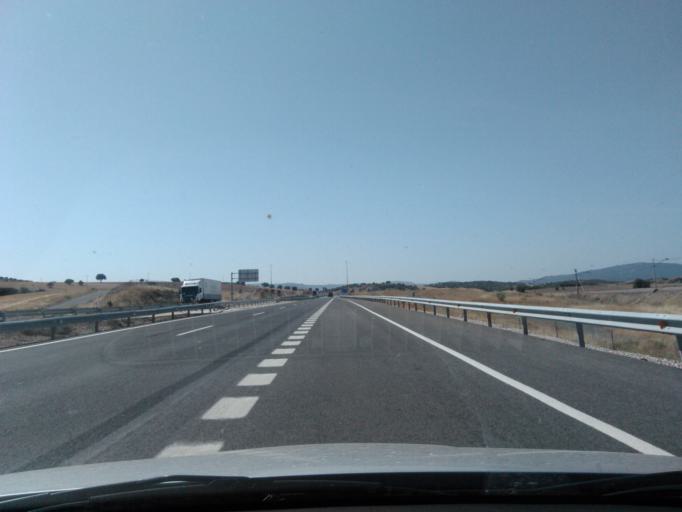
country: ES
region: Castille-La Mancha
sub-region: Provincia de Ciudad Real
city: Viso del Marques
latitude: 38.4919
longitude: -3.5026
